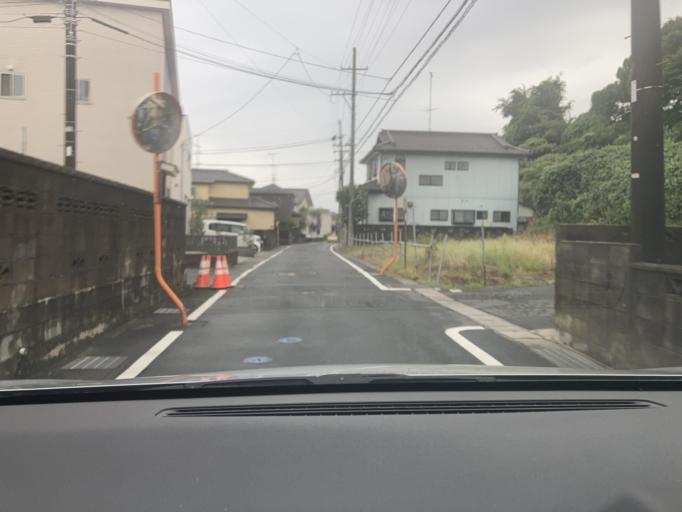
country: JP
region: Fukushima
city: Iwaki
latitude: 36.9638
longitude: 140.9030
